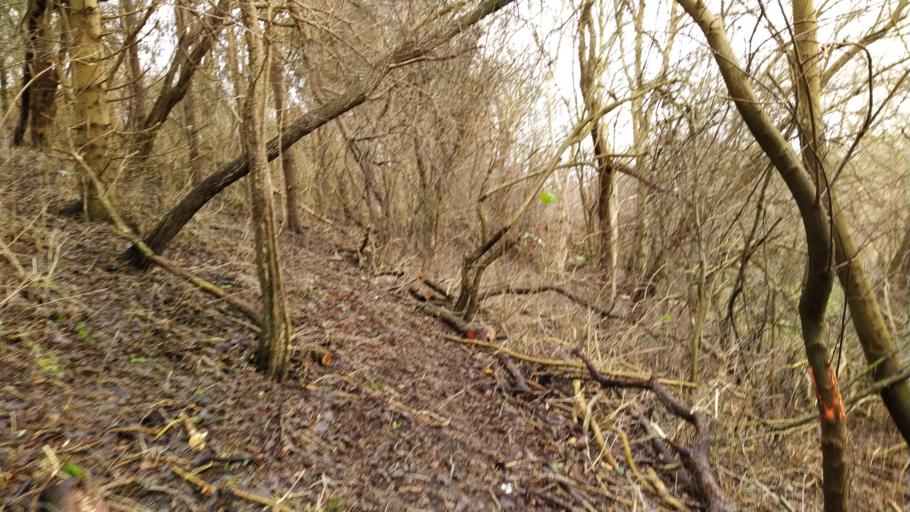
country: DK
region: Capital Region
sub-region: Egedal Kommune
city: Stenlose
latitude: 55.7627
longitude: 12.2111
